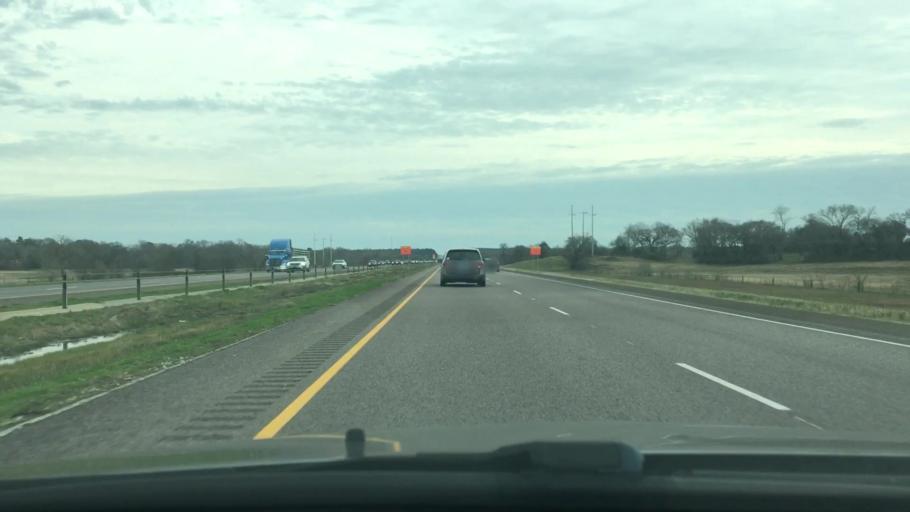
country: US
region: Texas
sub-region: Madison County
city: Madisonville
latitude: 30.9025
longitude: -95.7838
